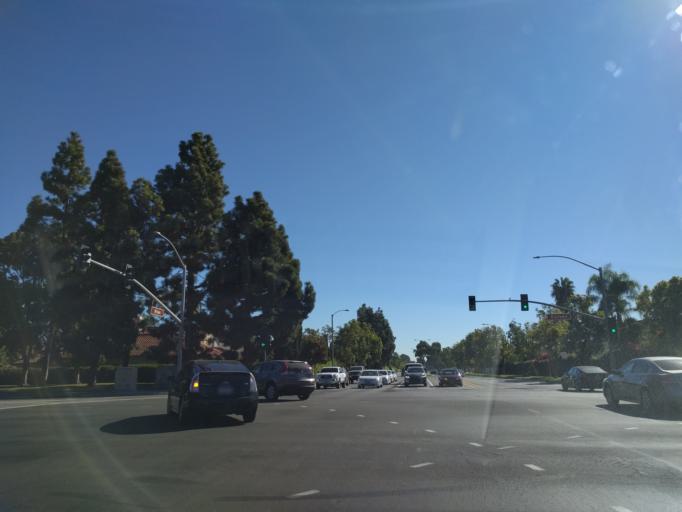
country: US
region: California
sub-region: Orange County
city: North Tustin
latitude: 33.7162
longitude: -117.7765
